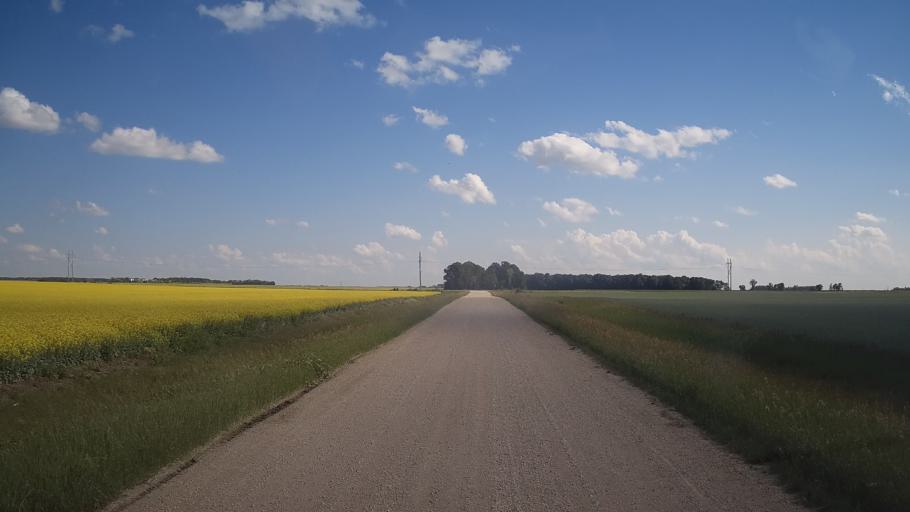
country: CA
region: Manitoba
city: Stonewall
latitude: 50.1258
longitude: -97.5054
